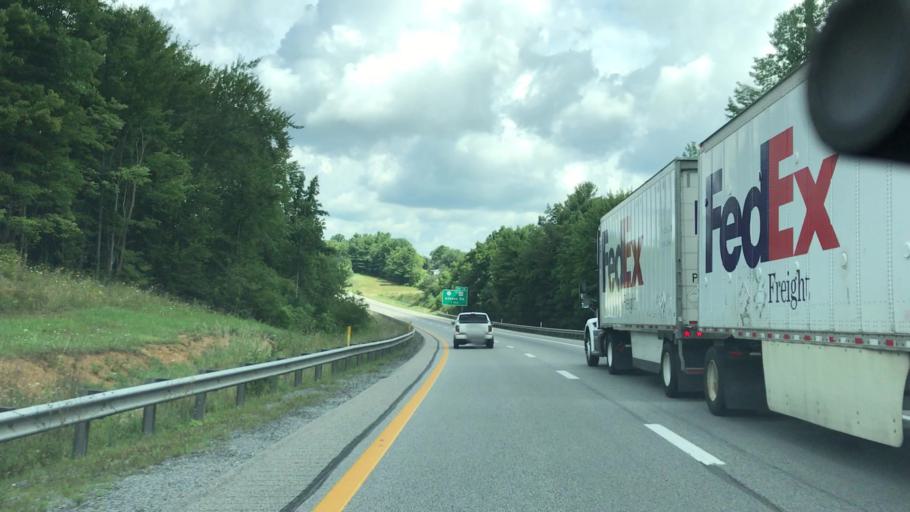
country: US
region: West Virginia
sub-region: Mercer County
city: Athens
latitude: 37.4050
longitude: -81.0608
